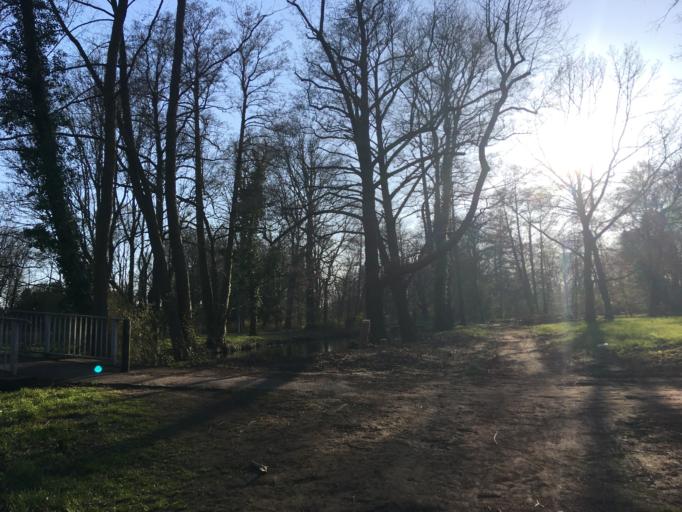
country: DE
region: Berlin
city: Buch
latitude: 52.6376
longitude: 13.4987
